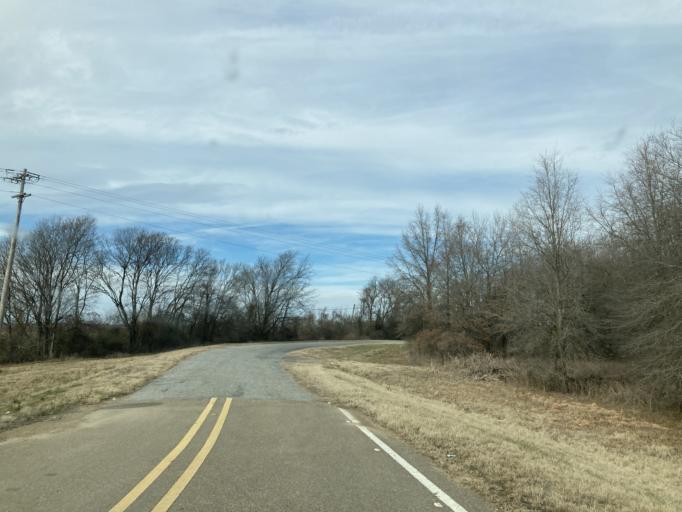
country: US
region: Mississippi
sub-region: Humphreys County
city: Belzoni
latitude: 33.1828
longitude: -90.6324
